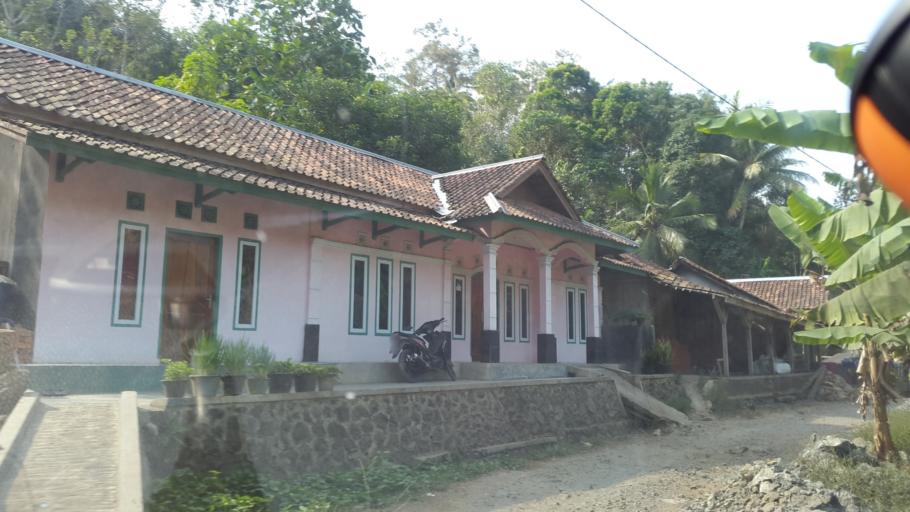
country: ID
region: West Java
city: Cigina
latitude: -7.2929
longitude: 106.8506
